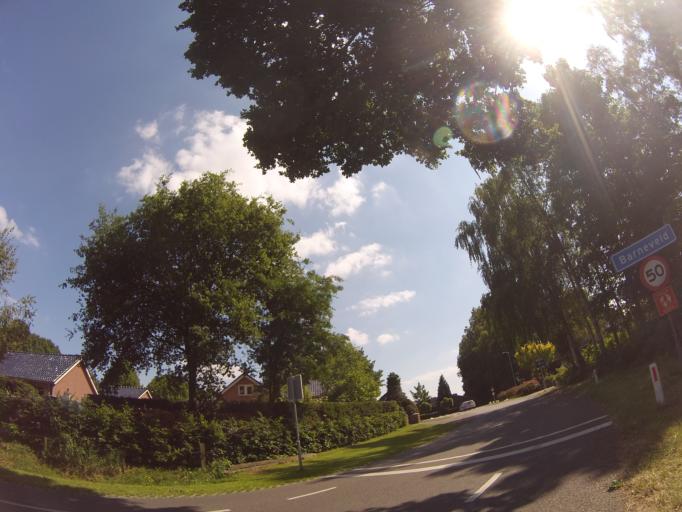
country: NL
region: Gelderland
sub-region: Gemeente Barneveld
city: Barneveld
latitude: 52.1424
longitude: 5.5611
